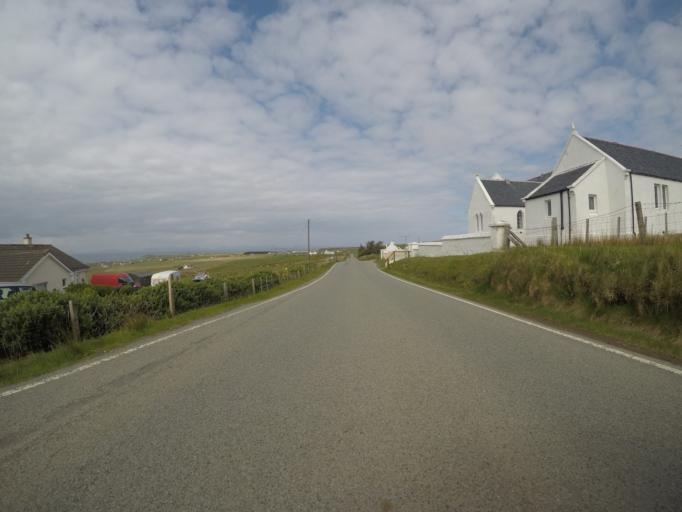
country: GB
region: Scotland
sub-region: Highland
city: Portree
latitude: 57.6381
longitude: -6.3764
